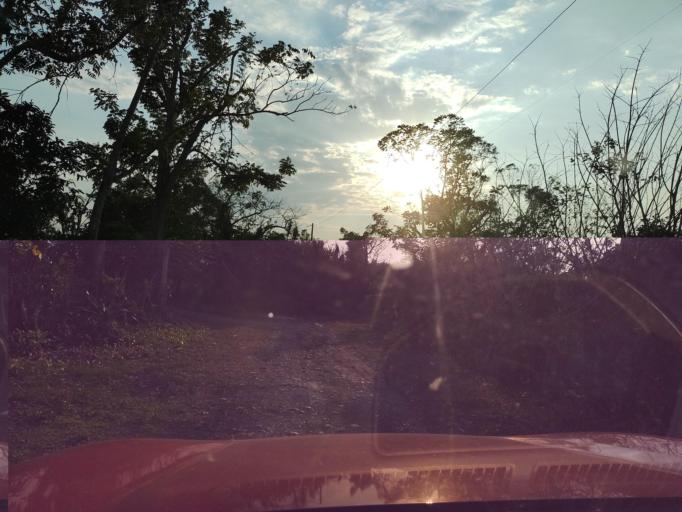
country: MX
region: Veracruz
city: Agua Dulce
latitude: 20.4012
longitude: -97.2914
